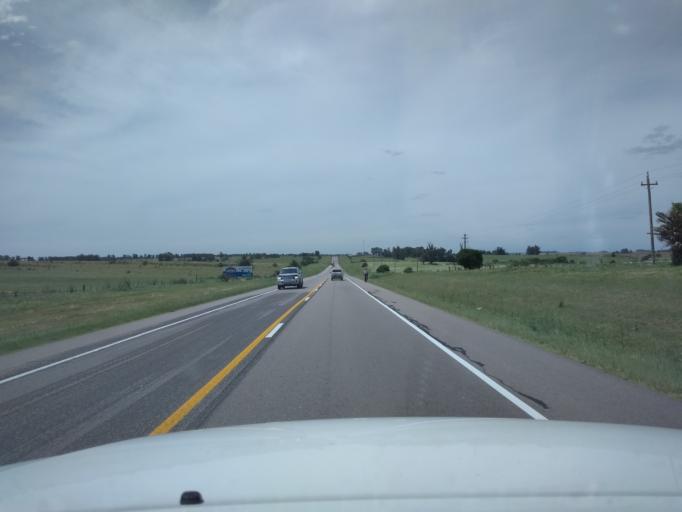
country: UY
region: Florida
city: Florida
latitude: -34.2240
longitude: -56.2102
